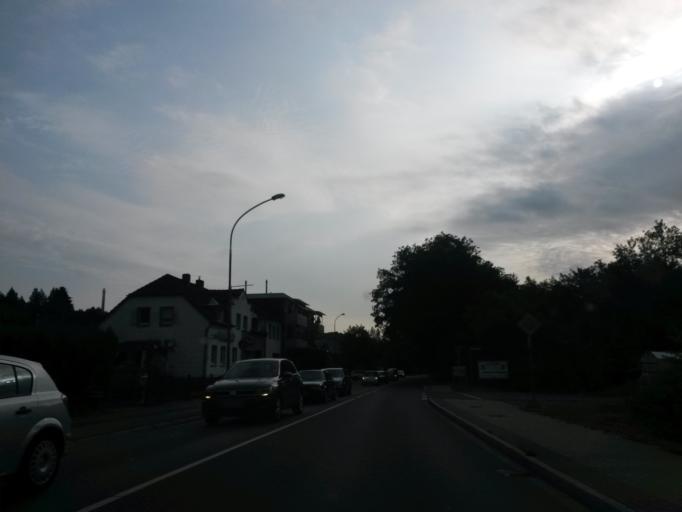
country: DE
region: North Rhine-Westphalia
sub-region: Regierungsbezirk Koln
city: Overath
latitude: 50.9586
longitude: 7.2356
